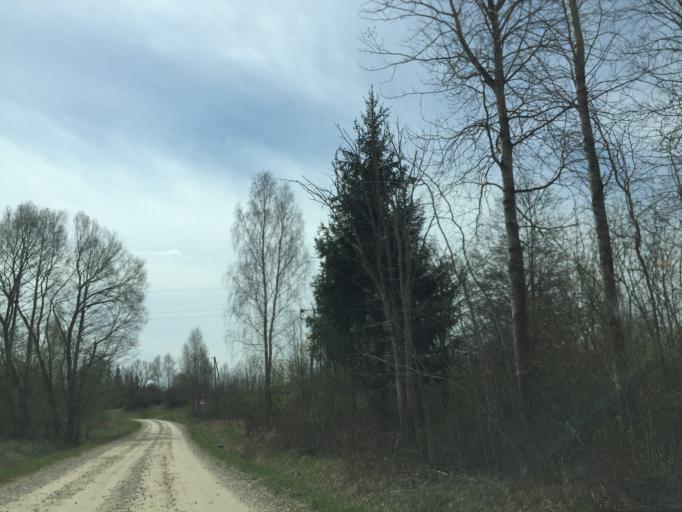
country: LV
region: Ludzas Rajons
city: Ludza
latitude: 56.5380
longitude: 27.5278
